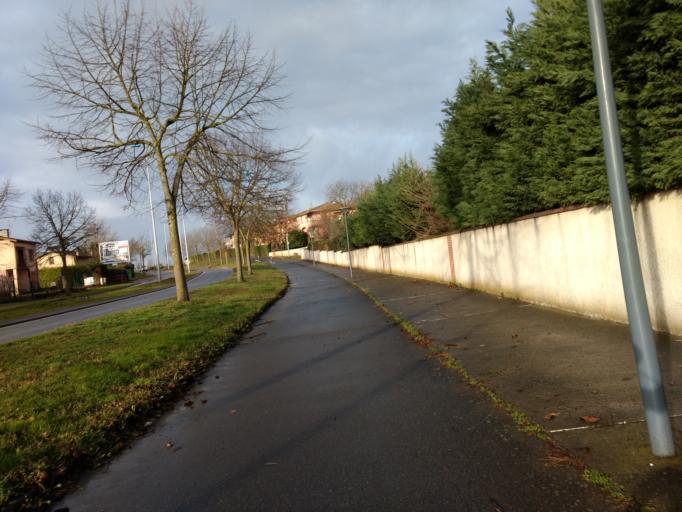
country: FR
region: Midi-Pyrenees
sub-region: Departement de la Haute-Garonne
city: Colomiers
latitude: 43.6126
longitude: 1.3172
